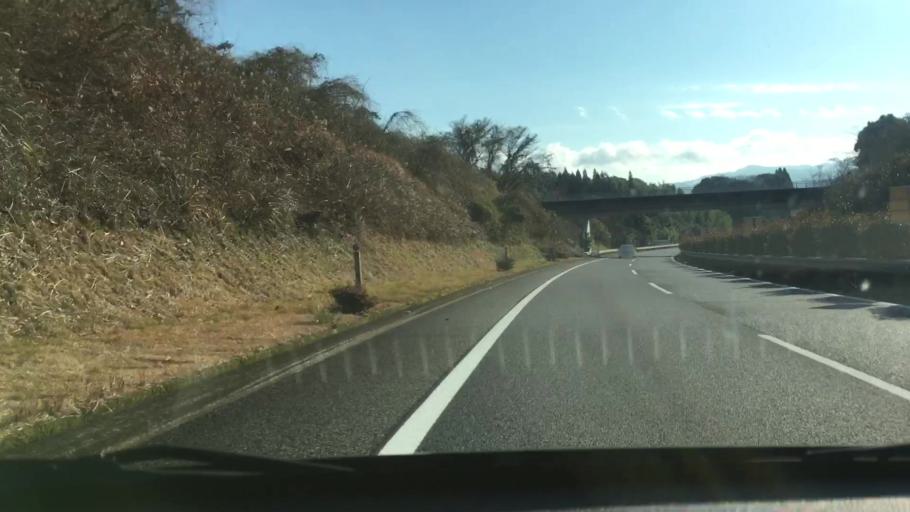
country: JP
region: Kumamoto
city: Hitoyoshi
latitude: 32.2195
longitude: 130.7803
